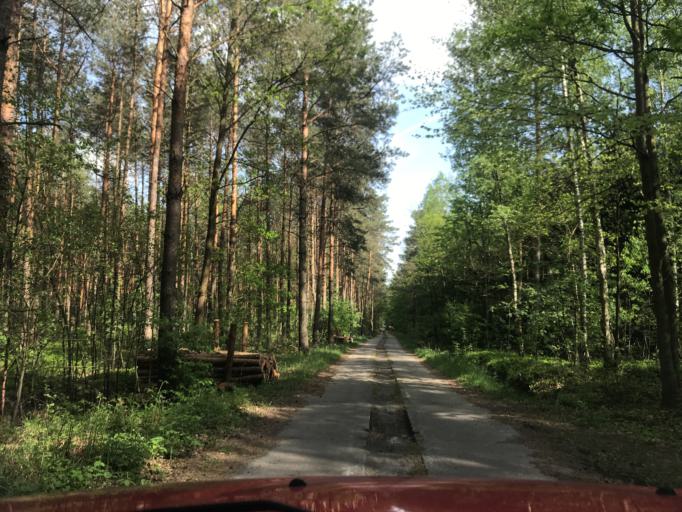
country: PL
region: Greater Poland Voivodeship
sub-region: Powiat kaliski
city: Stawiszyn
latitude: 51.9400
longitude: 18.1585
